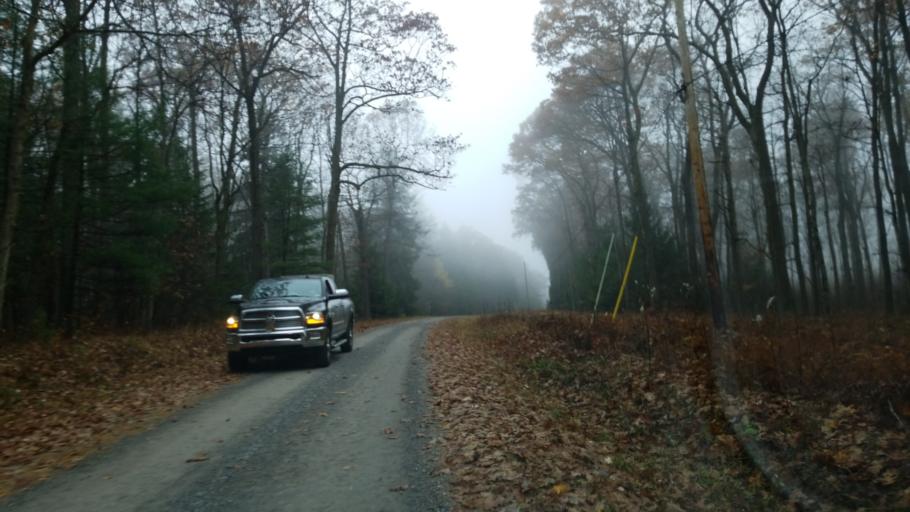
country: US
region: Pennsylvania
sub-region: Clearfield County
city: Clearfield
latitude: 41.1015
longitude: -78.5265
